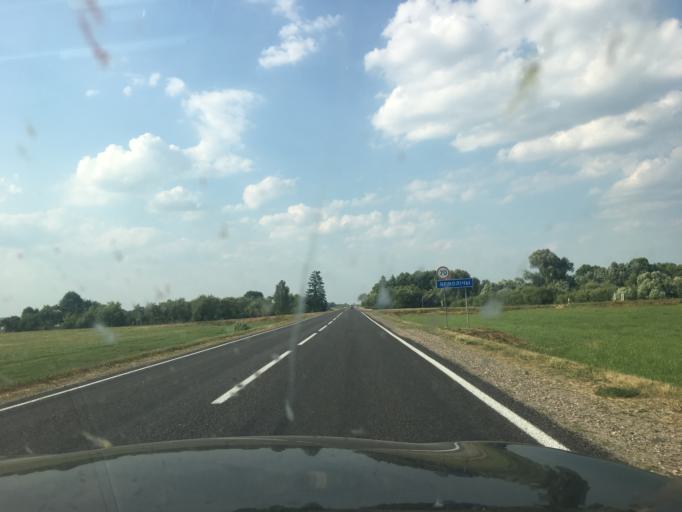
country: BY
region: Grodnenskaya
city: Indura
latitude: 53.3877
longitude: 23.9510
